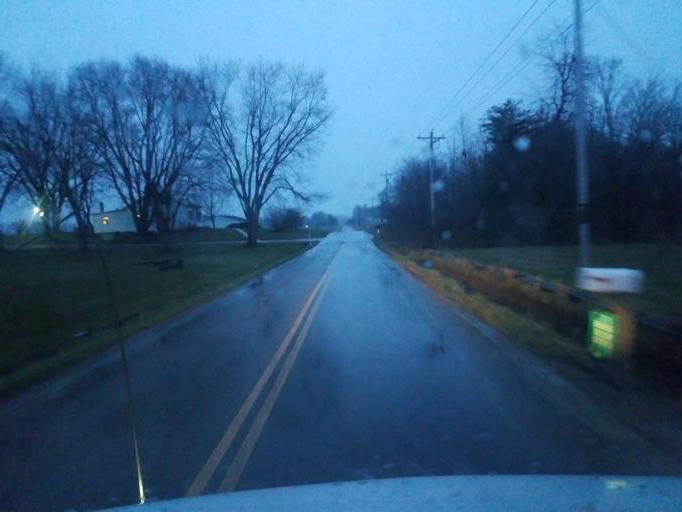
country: US
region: Ohio
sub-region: Knox County
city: Mount Vernon
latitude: 40.3213
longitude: -82.4567
